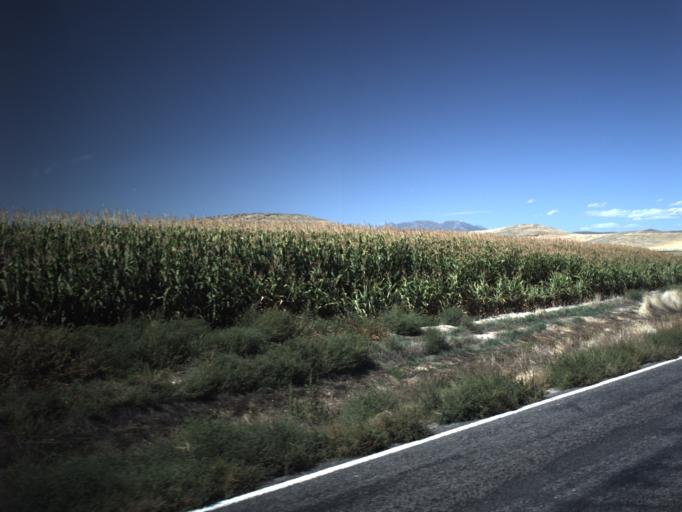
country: US
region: Utah
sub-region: Utah County
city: Genola
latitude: 40.1020
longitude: -111.9591
